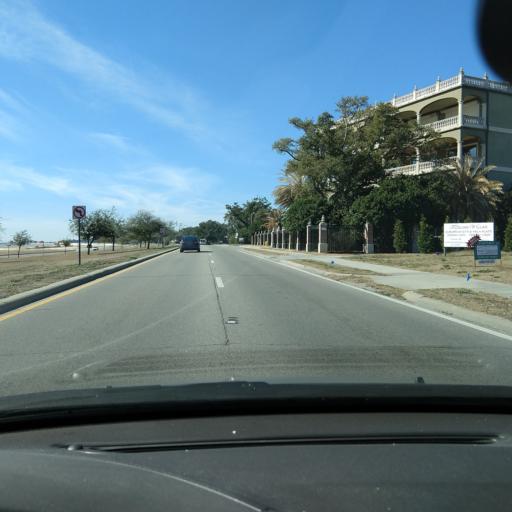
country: US
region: Mississippi
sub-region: Harrison County
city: Gulfport
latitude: 30.3570
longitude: -89.1167
